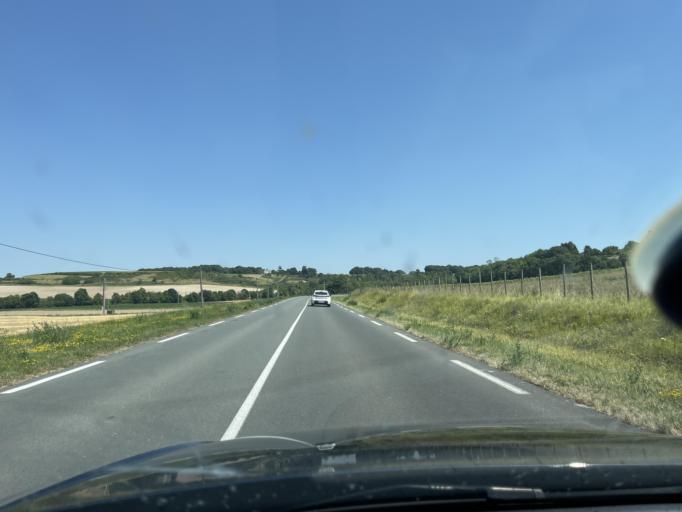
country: FR
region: Poitou-Charentes
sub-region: Departement de la Charente-Maritime
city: Mirambeau
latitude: 45.4117
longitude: -0.6125
